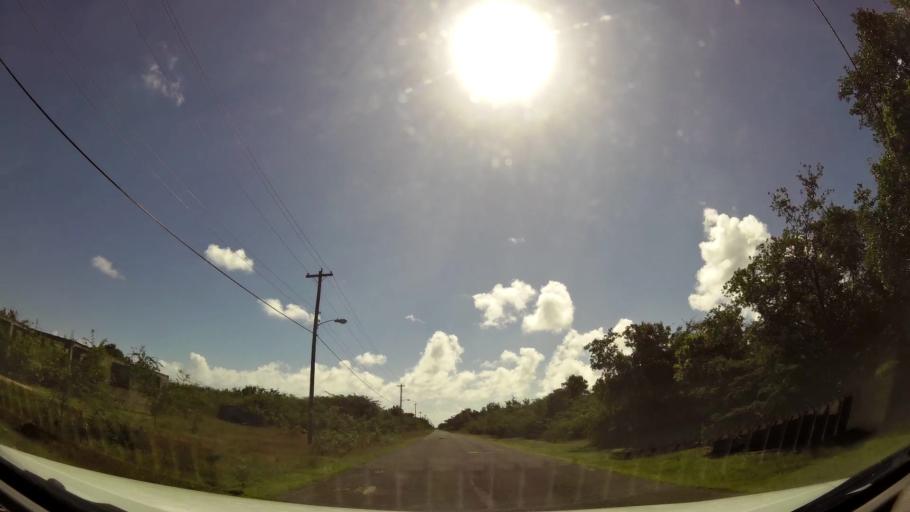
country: AG
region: Barbuda
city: Codrington
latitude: 17.6152
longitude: -61.8283
